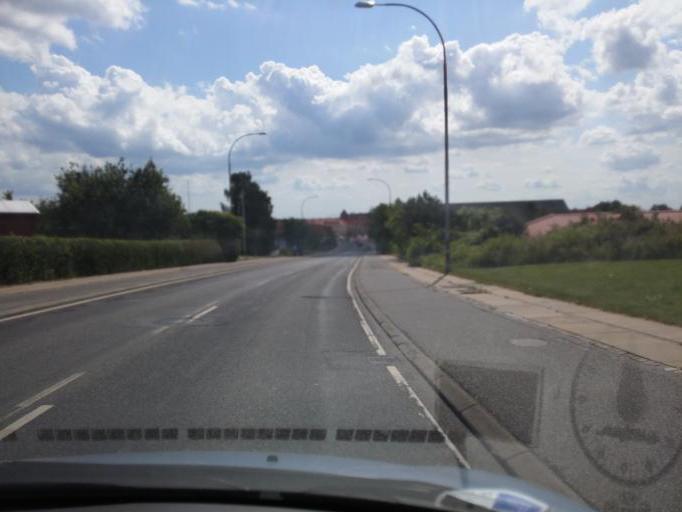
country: DK
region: South Denmark
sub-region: Kerteminde Kommune
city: Kerteminde
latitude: 55.4530
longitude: 10.6531
